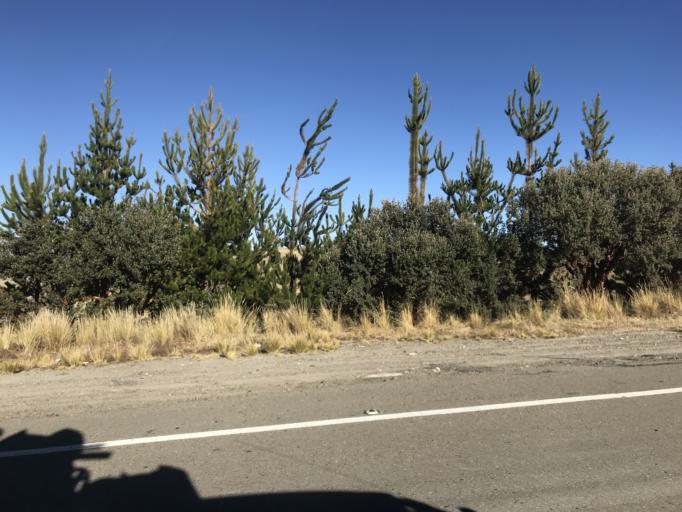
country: PE
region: Puno
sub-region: Yunguyo
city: Yunguyo
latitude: -16.1676
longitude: -68.9851
